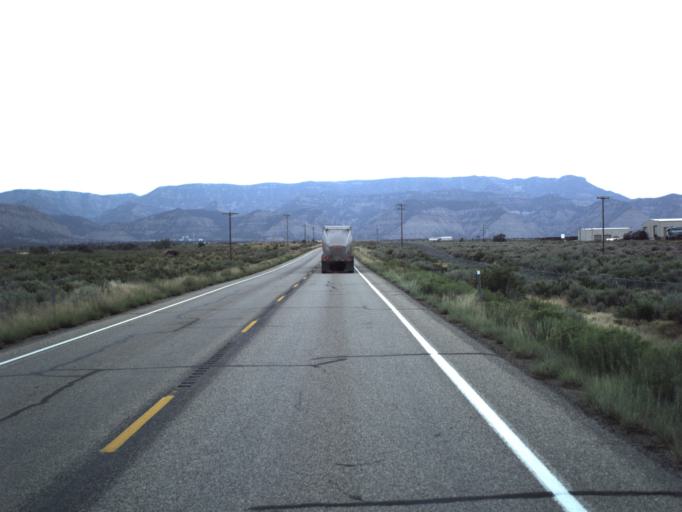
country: US
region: Utah
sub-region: Carbon County
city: East Carbon City
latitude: 39.5356
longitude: -110.4775
